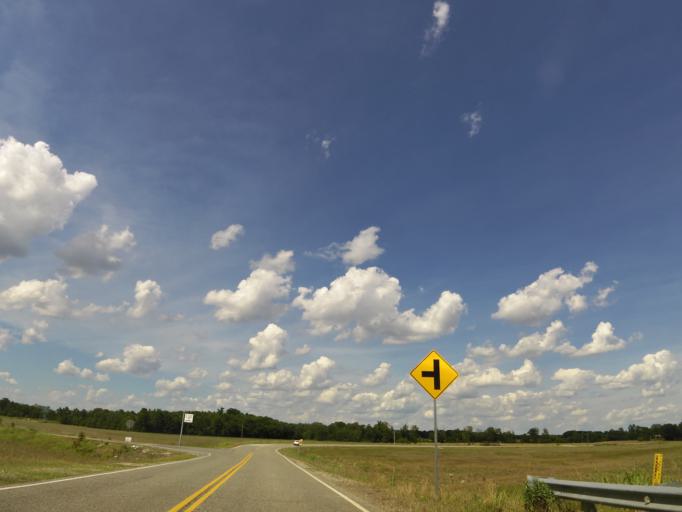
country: US
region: Tennessee
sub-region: Gibson County
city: Milan
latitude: 35.9791
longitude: -88.7716
